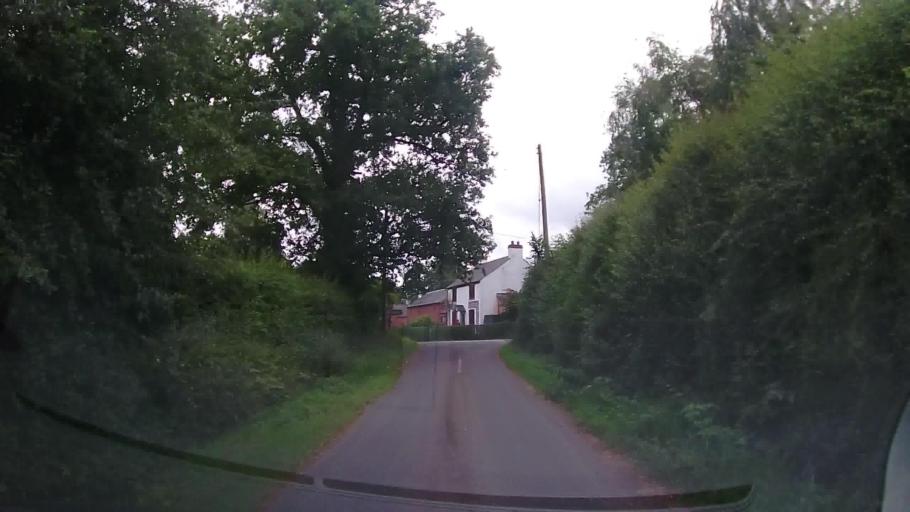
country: GB
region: England
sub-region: Shropshire
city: Prees
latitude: 52.9058
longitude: -2.7062
